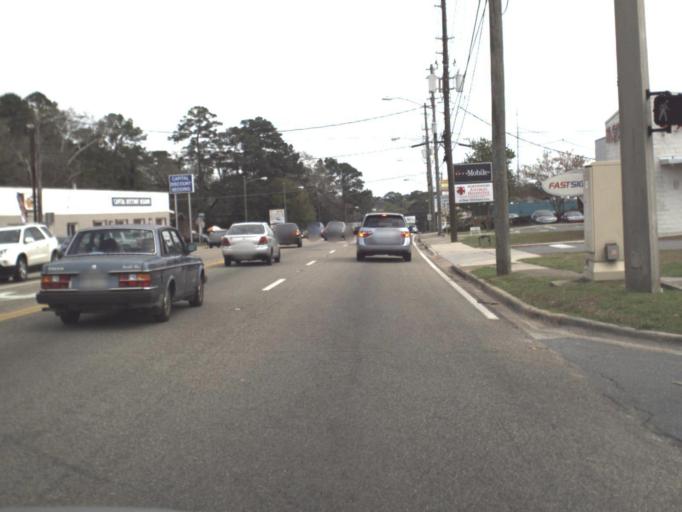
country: US
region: Florida
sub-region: Leon County
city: Tallahassee
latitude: 30.4662
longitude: -84.2842
